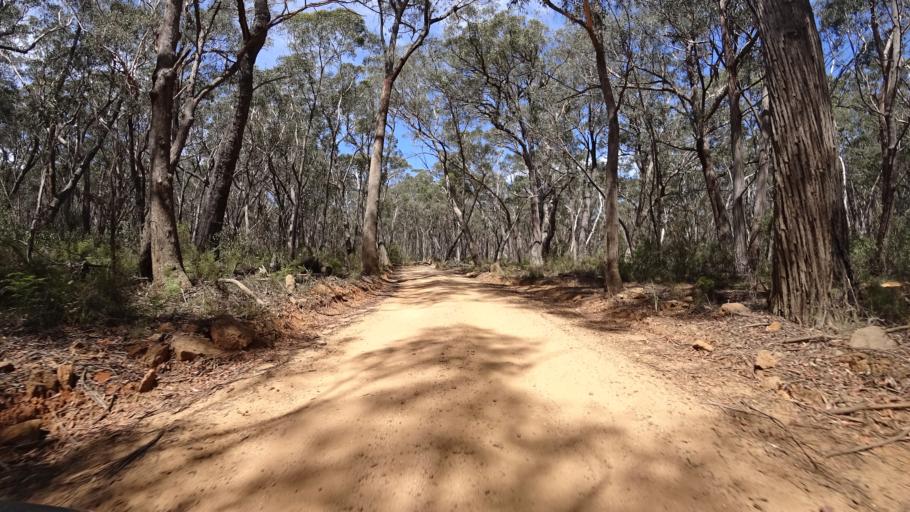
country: AU
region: New South Wales
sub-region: Lithgow
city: Lithgow
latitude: -33.2701
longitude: 150.2273
